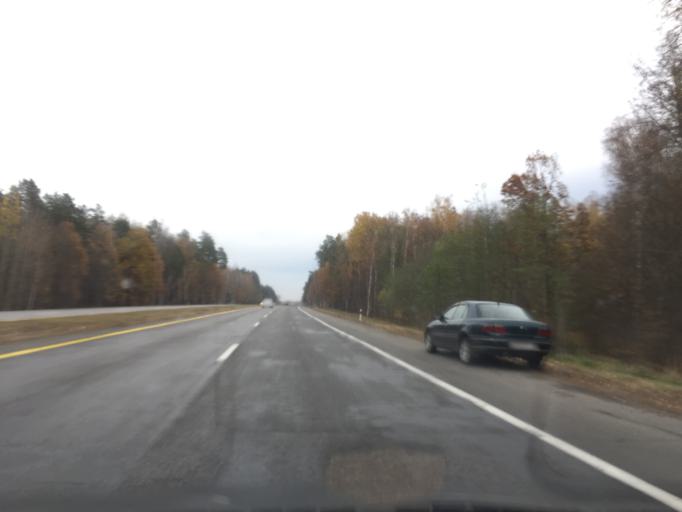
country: BY
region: Gomel
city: Horad Rechytsa
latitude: 52.3600
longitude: 30.6559
